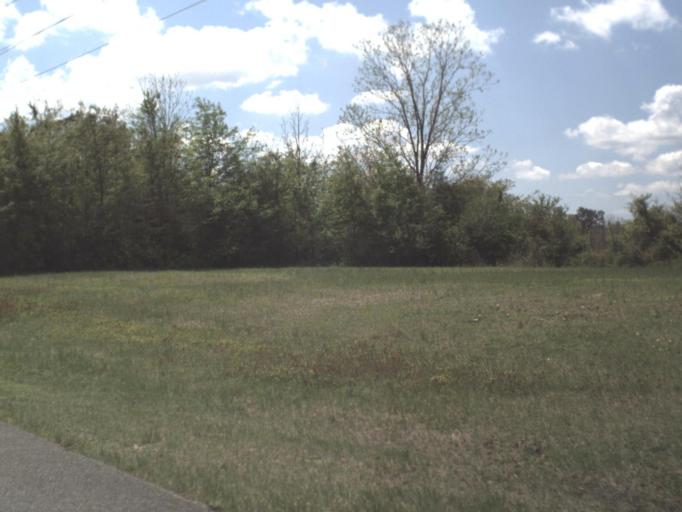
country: US
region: Florida
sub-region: Okaloosa County
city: Crestview
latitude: 30.8850
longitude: -86.6633
